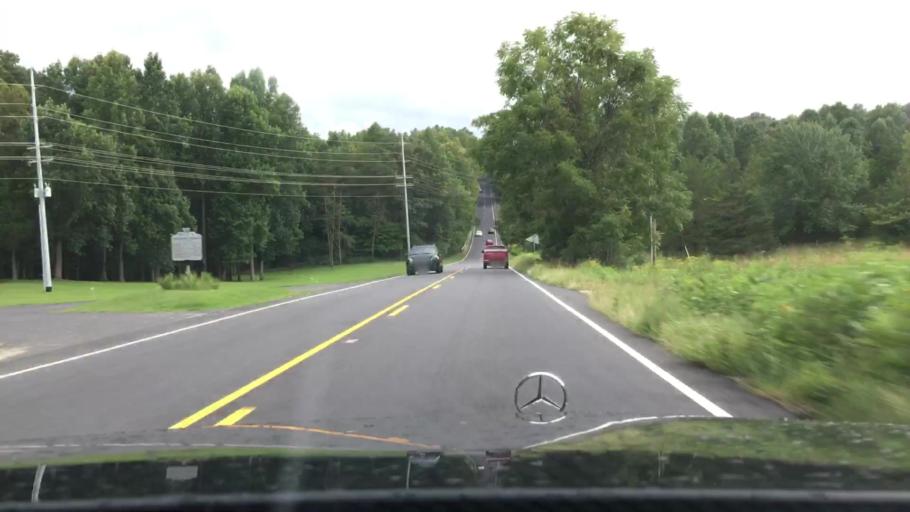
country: US
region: Virginia
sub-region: Nelson County
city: Nellysford
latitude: 37.9122
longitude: -78.8455
